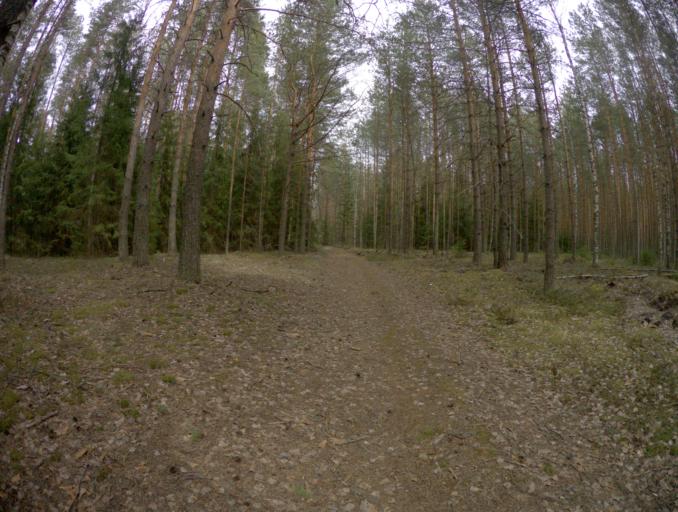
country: RU
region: Vladimir
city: Raduzhnyy
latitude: 55.9317
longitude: 40.2734
